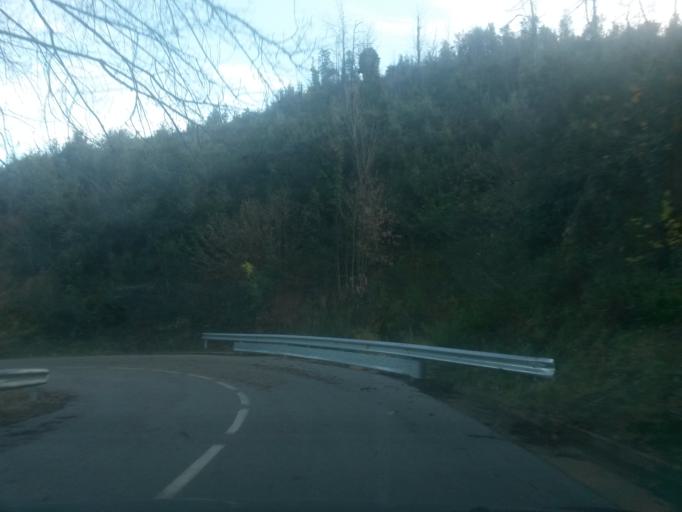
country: ES
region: Catalonia
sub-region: Provincia de Girona
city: Sant Hilari Sacalm
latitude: 41.8624
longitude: 2.5688
